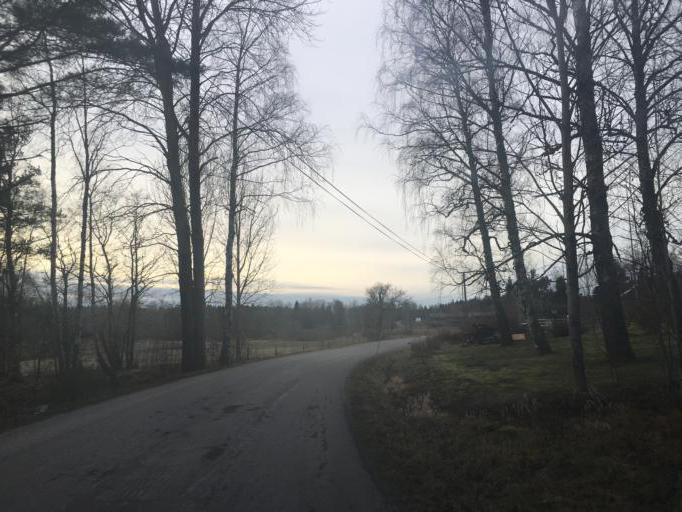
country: SE
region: OEstergoetland
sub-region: Norrkopings Kommun
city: Kimstad
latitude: 58.4287
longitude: 16.0693
